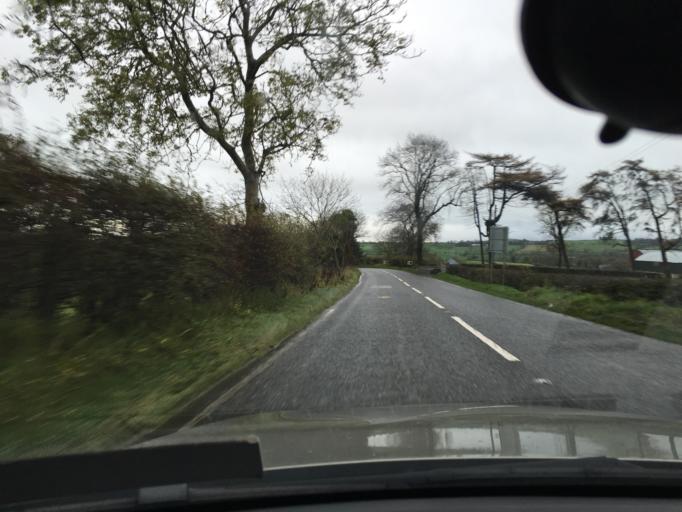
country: GB
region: Northern Ireland
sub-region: Larne District
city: Larne
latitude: 54.8329
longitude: -5.8884
